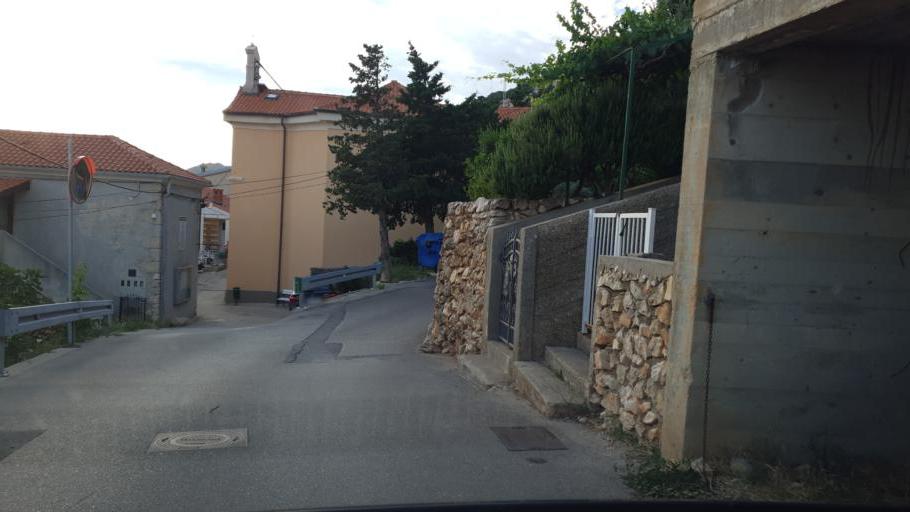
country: HR
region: Primorsko-Goranska
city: Punat
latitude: 44.9600
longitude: 14.6864
